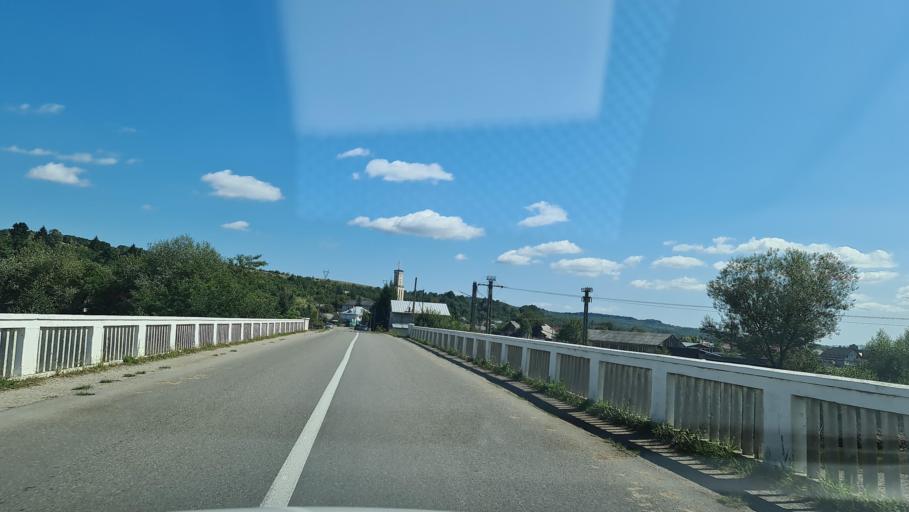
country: RO
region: Bacau
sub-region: Comuna Balcani
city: Frumoasa
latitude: 46.6638
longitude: 26.5355
